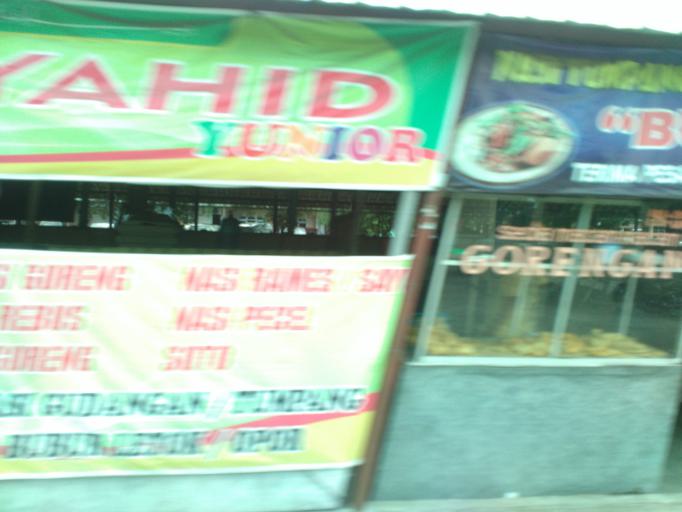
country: ID
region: Central Java
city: Klaten
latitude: -7.6852
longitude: 110.6349
